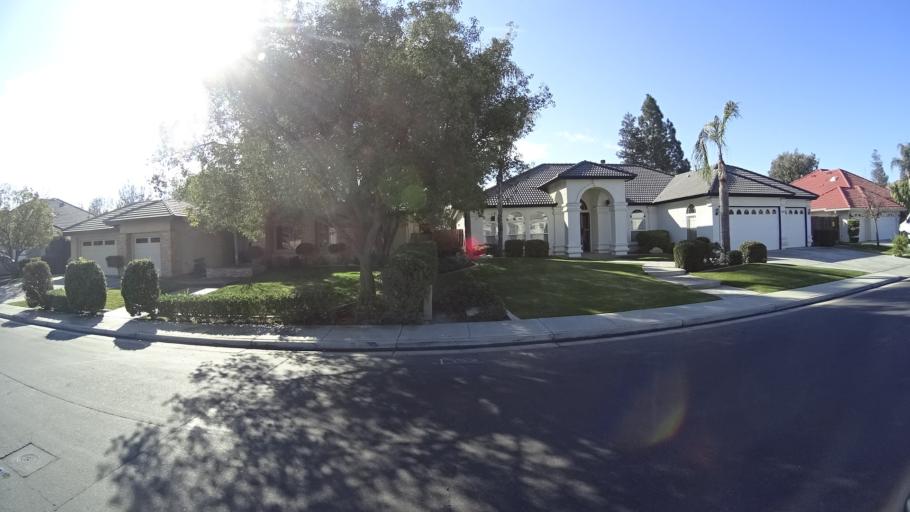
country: US
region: California
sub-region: Kern County
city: Greenacres
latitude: 35.3429
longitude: -119.1183
